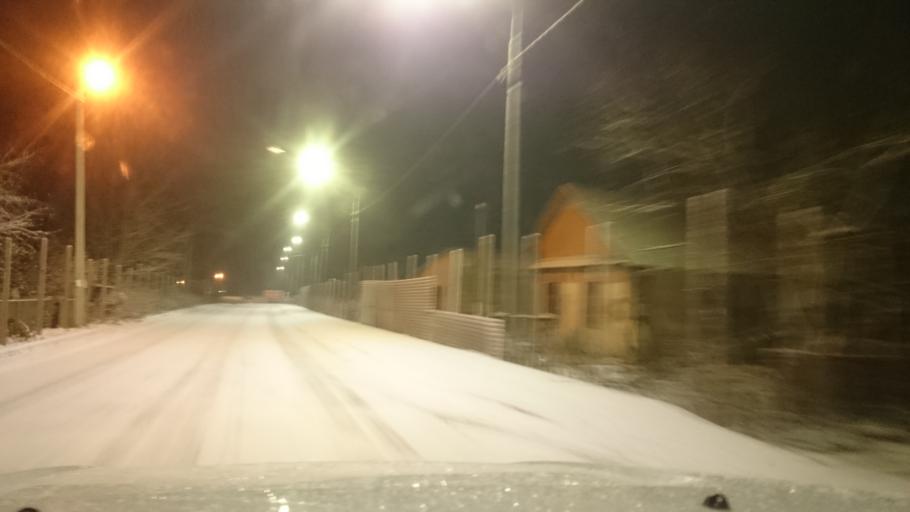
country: RU
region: Tula
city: Kosaya Gora
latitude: 54.1871
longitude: 37.5172
